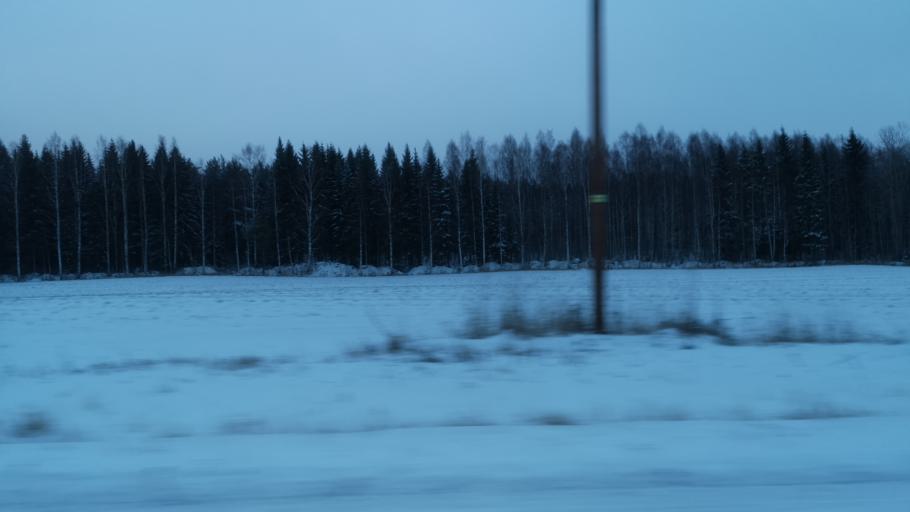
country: FI
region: Southern Savonia
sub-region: Savonlinna
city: Enonkoski
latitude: 62.0883
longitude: 28.6811
